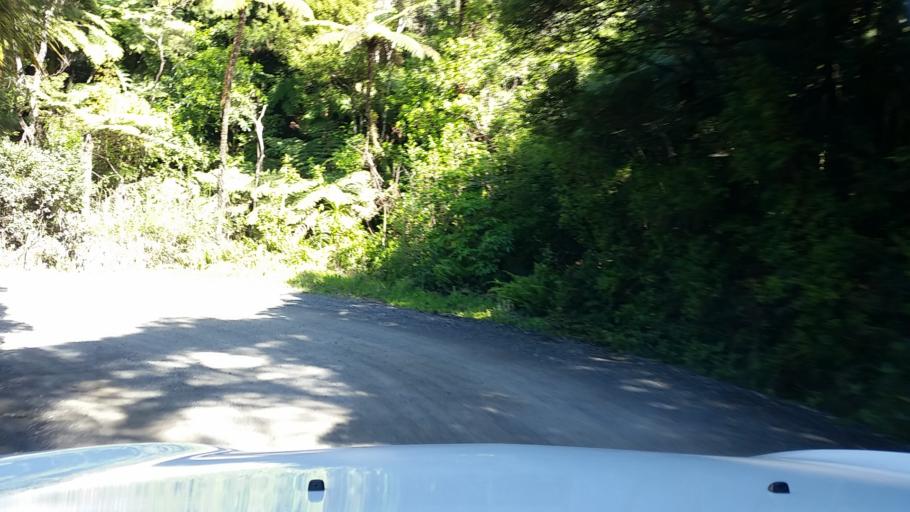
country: NZ
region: Auckland
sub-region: Auckland
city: Titirangi
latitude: -37.0225
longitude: 174.5360
